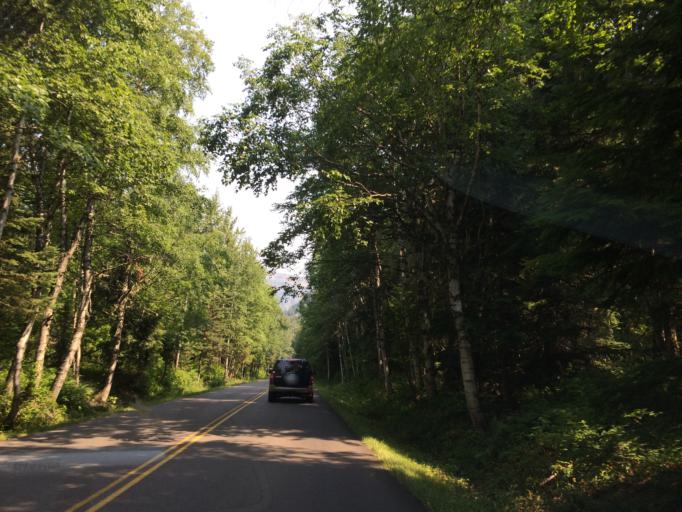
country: US
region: Montana
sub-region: Flathead County
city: Columbia Falls
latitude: 48.6770
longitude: -113.8208
